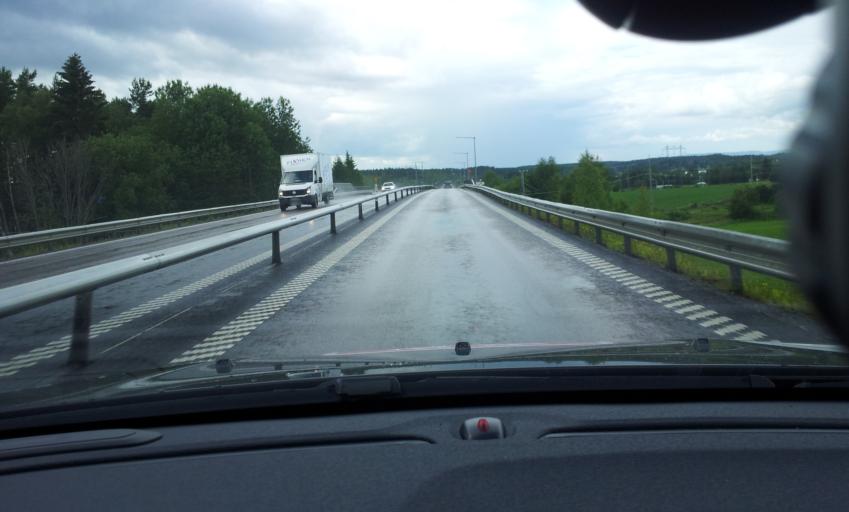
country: SE
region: Jaemtland
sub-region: Krokoms Kommun
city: Krokom
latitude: 63.3132
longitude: 14.4665
